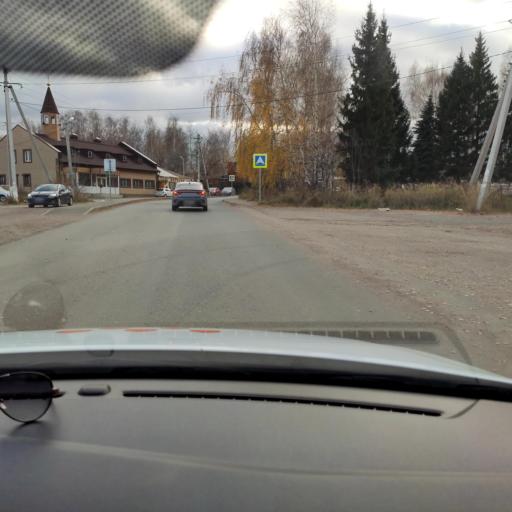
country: RU
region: Tatarstan
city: Stolbishchi
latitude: 55.7419
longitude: 49.2732
